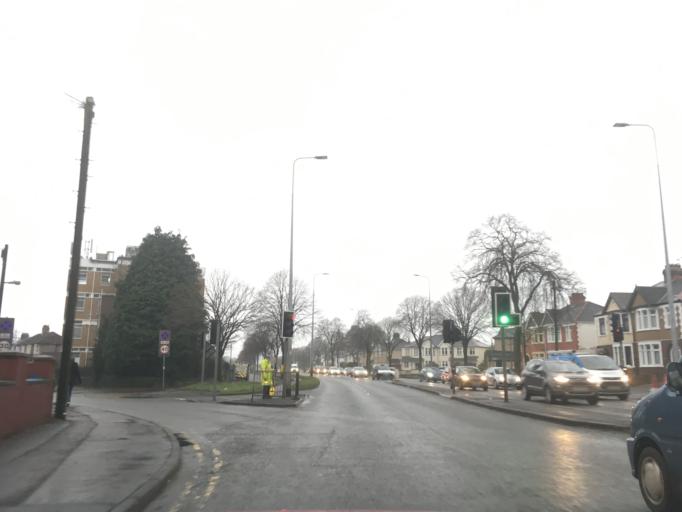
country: GB
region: Wales
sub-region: Cardiff
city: Cardiff
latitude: 51.4908
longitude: -3.2220
